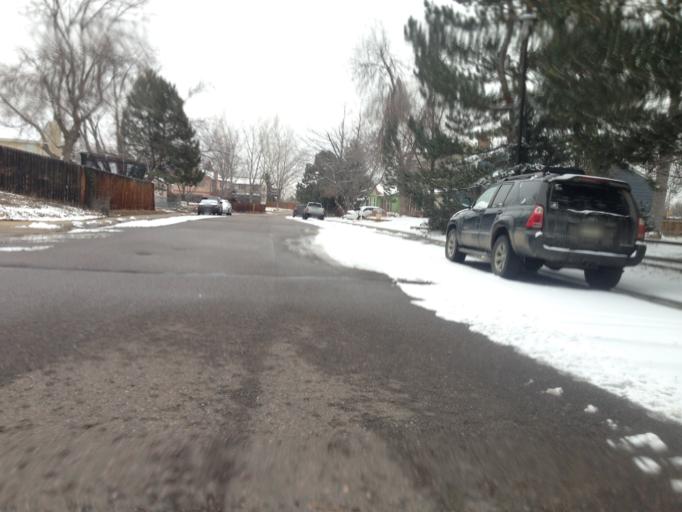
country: US
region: Colorado
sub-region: Boulder County
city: Louisville
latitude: 39.9835
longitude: -105.1397
